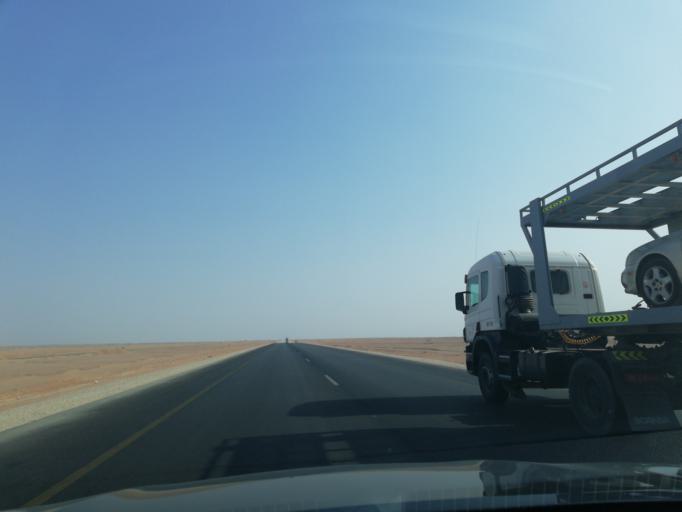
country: OM
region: Zufar
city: Salalah
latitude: 17.8360
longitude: 54.0032
